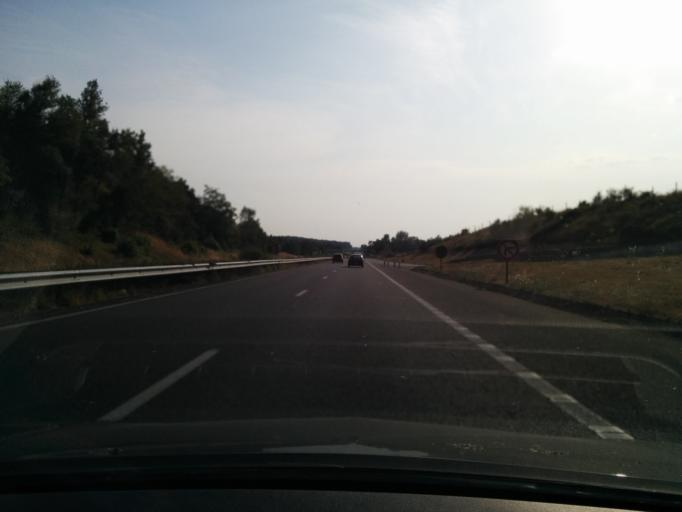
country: FR
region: Midi-Pyrenees
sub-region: Departement du Tarn
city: Montans
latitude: 43.8510
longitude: 1.8800
